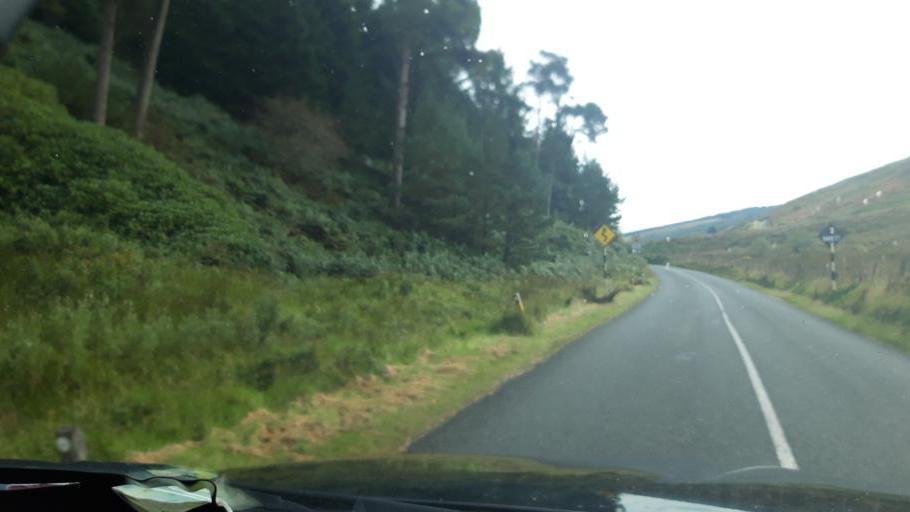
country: IE
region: Leinster
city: Ballinteer
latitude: 53.2339
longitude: -6.2792
